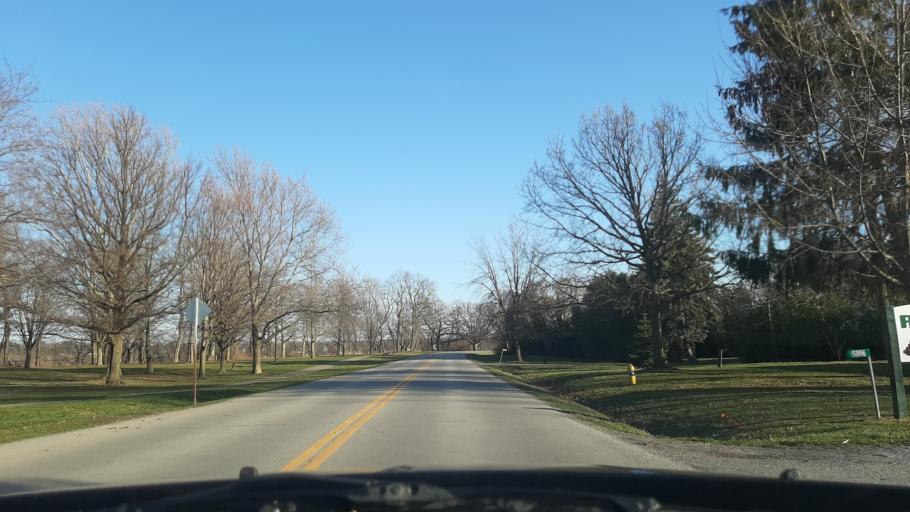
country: US
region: New York
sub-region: Niagara County
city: Youngstown
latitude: 43.2307
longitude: -79.0608
